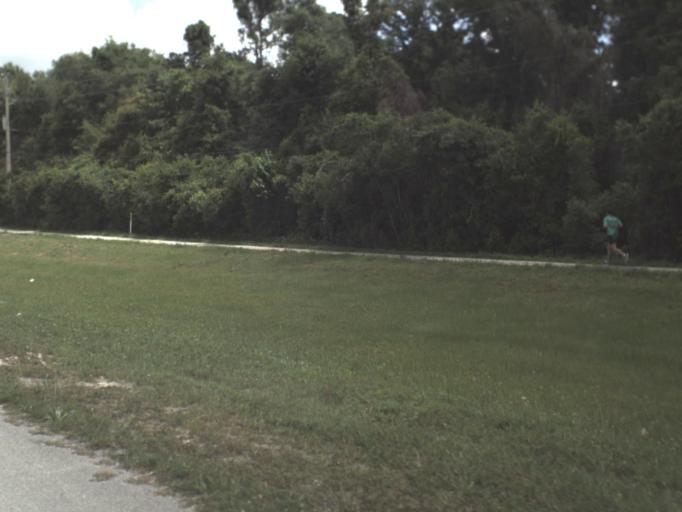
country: US
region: Florida
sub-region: Duval County
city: Jacksonville
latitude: 30.2326
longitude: -81.5519
